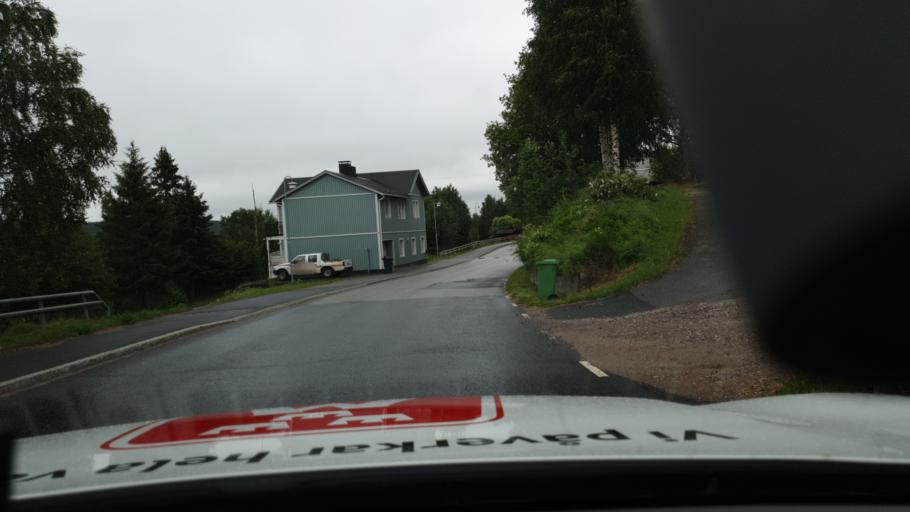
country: SE
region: Norrbotten
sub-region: Overtornea Kommun
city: OEvertornea
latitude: 66.3944
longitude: 23.6516
